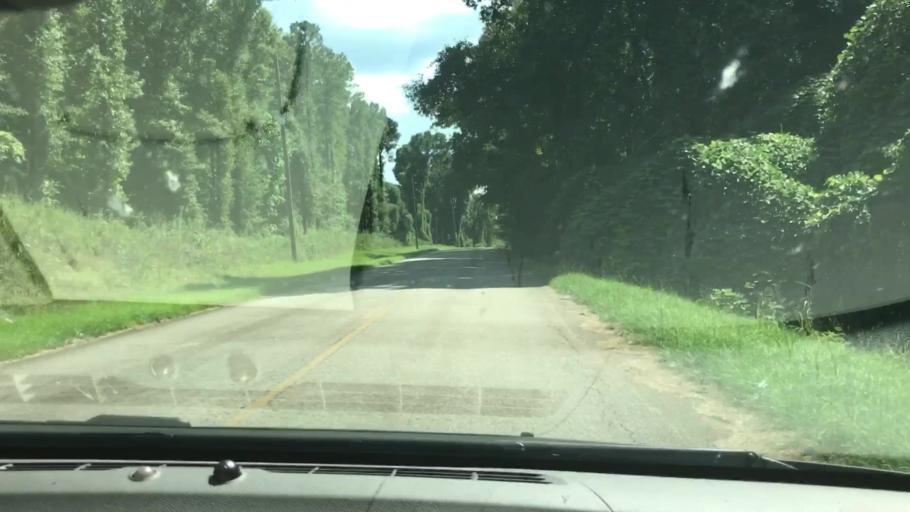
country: US
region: Georgia
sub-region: Troup County
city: La Grange
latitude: 33.0952
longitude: -85.1298
